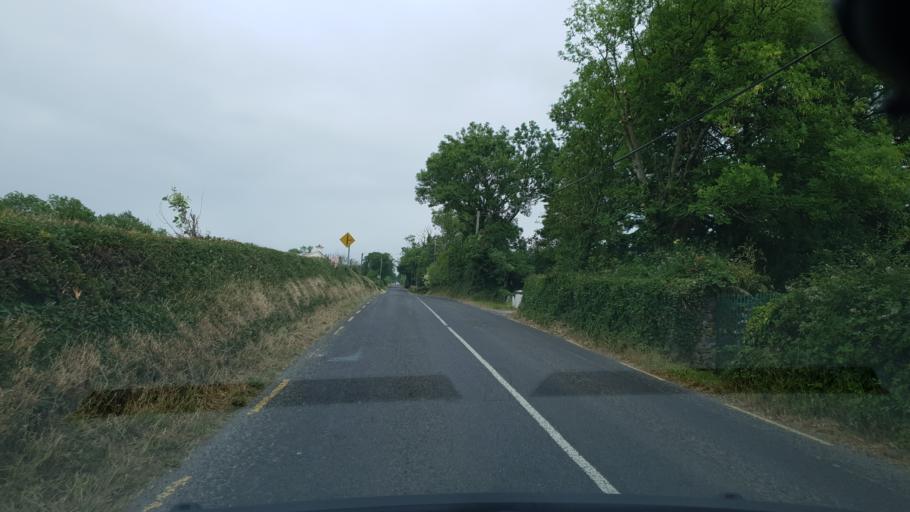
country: IE
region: Munster
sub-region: Ciarrai
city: Tralee
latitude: 52.1633
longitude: -9.6393
